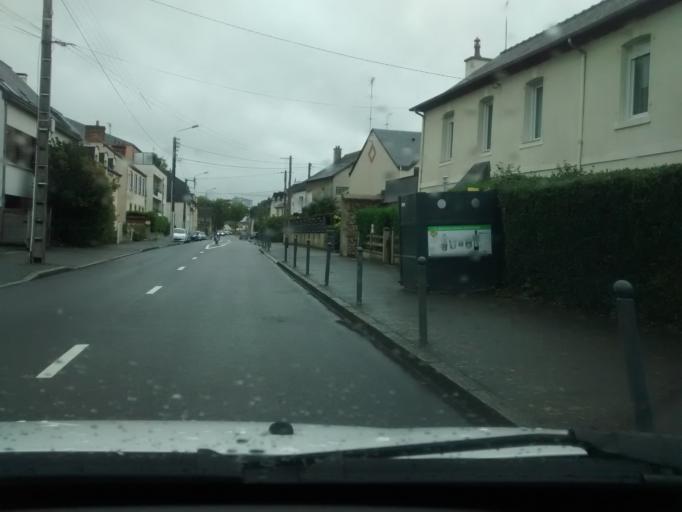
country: FR
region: Brittany
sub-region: Departement d'Ille-et-Vilaine
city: Rennes
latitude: 48.1286
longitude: -1.6730
